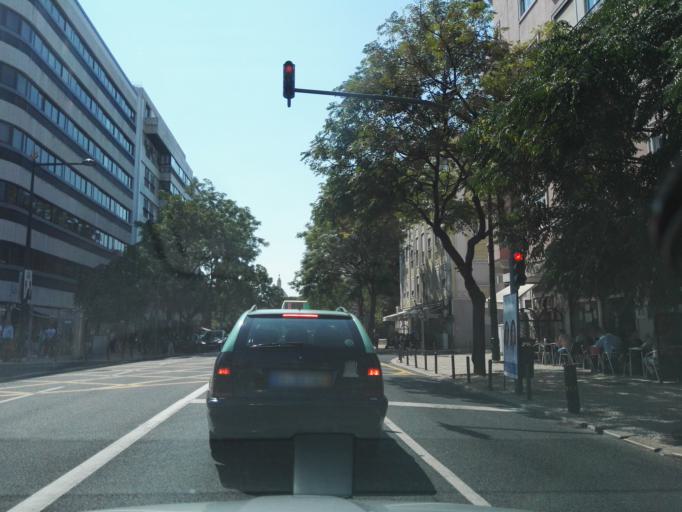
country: PT
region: Lisbon
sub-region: Lisbon
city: Lisbon
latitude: 38.7174
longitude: -9.1575
